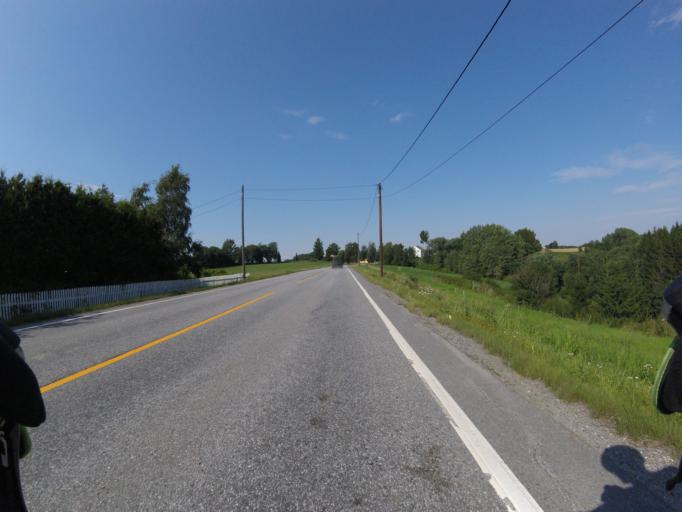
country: NO
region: Akershus
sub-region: Ullensaker
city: Klofta
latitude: 60.0524
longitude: 11.1183
